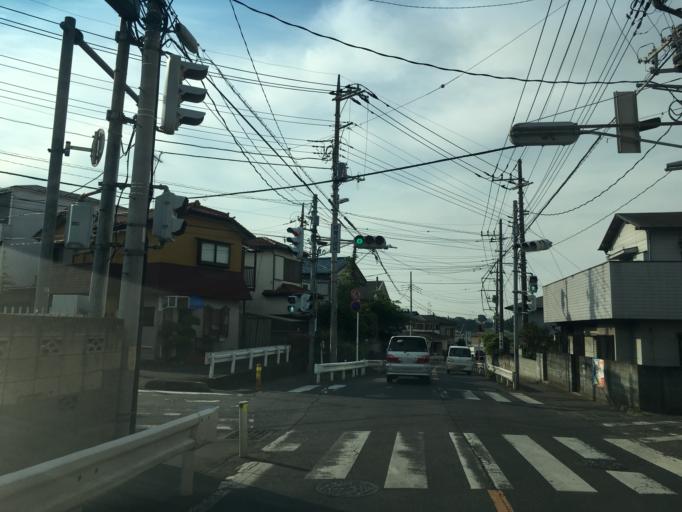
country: JP
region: Saitama
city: Tokorozawa
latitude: 35.7882
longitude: 139.5067
